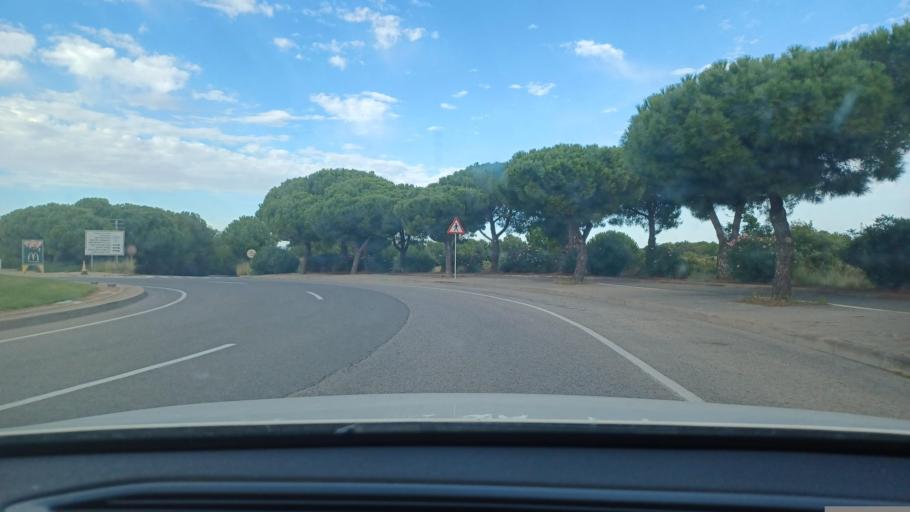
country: ES
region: Catalonia
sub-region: Provincia de Tarragona
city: Vila-seca
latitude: 41.0999
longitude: 1.1519
